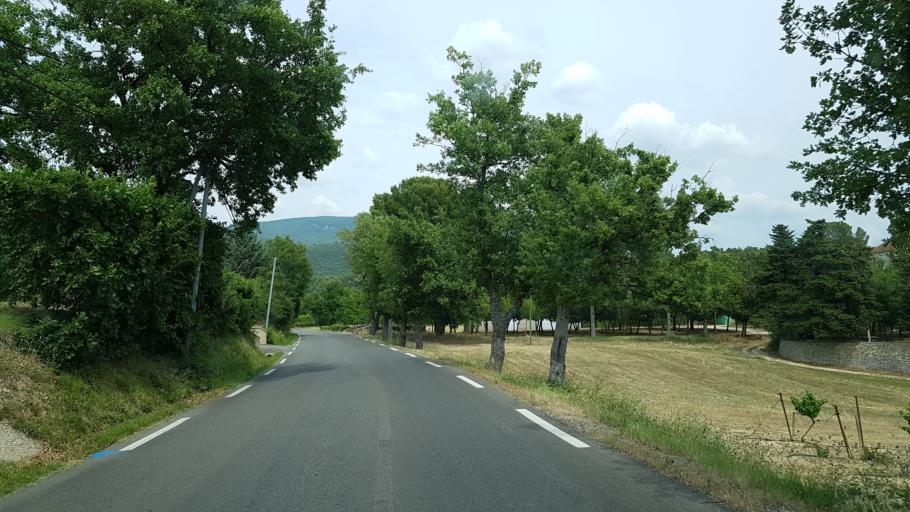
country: FR
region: Provence-Alpes-Cote d'Azur
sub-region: Departement du Vaucluse
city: Saint-Saturnin-les-Apt
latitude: 43.9333
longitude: 5.4215
